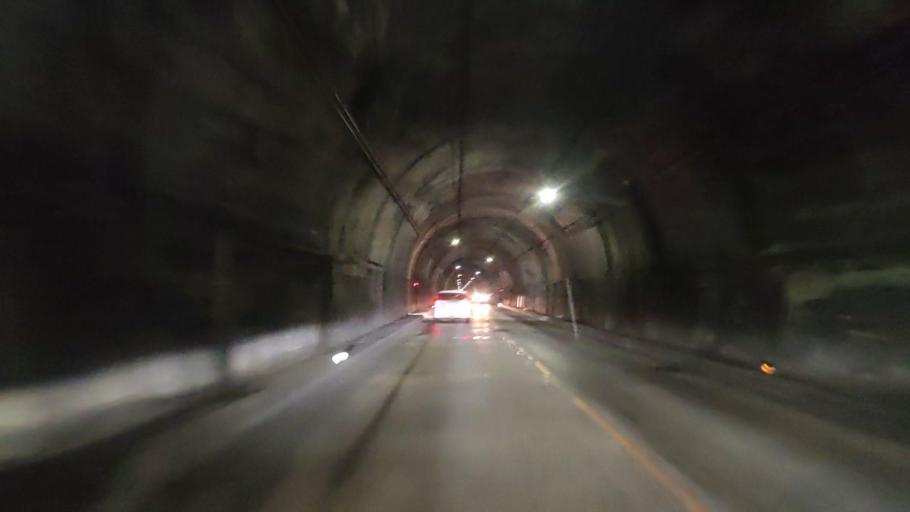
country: JP
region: Nara
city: Yoshino-cho
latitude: 34.3645
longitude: 135.9166
